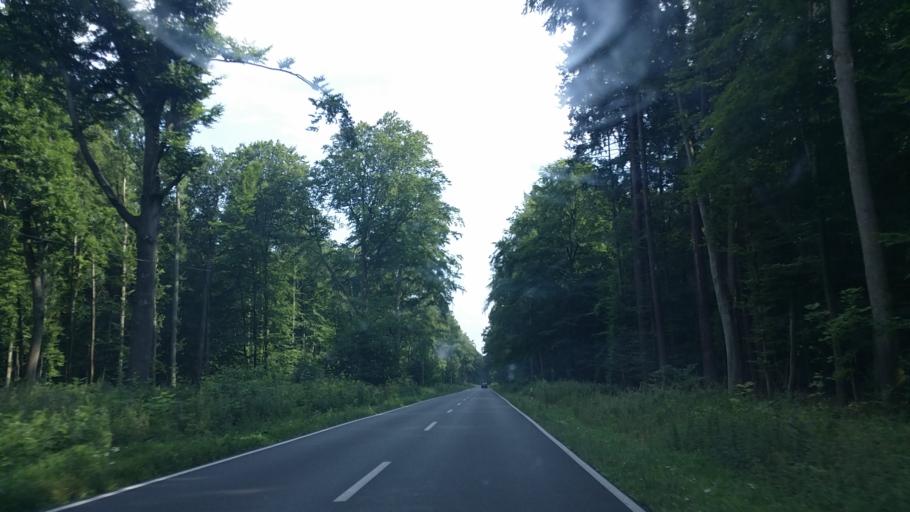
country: PL
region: West Pomeranian Voivodeship
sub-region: Powiat mysliborski
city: Barlinek
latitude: 52.9480
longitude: 15.1863
